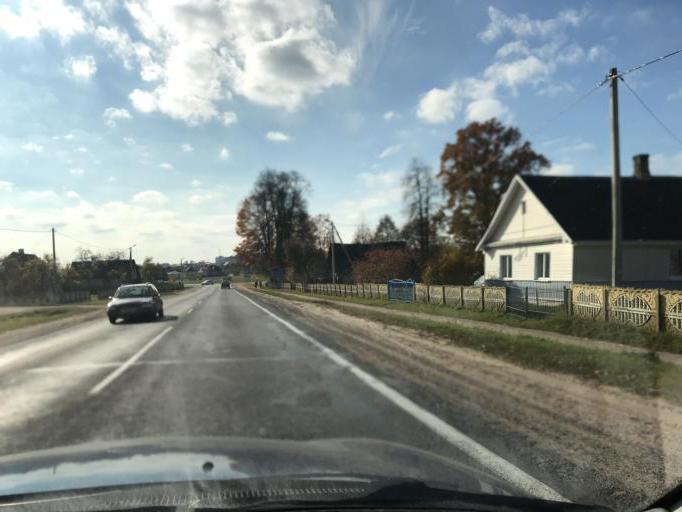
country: BY
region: Grodnenskaya
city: Voranava
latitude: 54.1588
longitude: 25.3267
